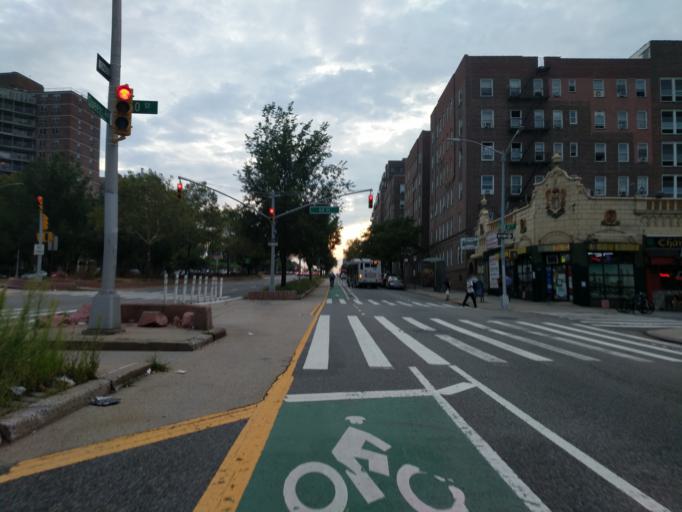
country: US
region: New York
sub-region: Queens County
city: Long Island City
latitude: 40.7417
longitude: -73.9043
